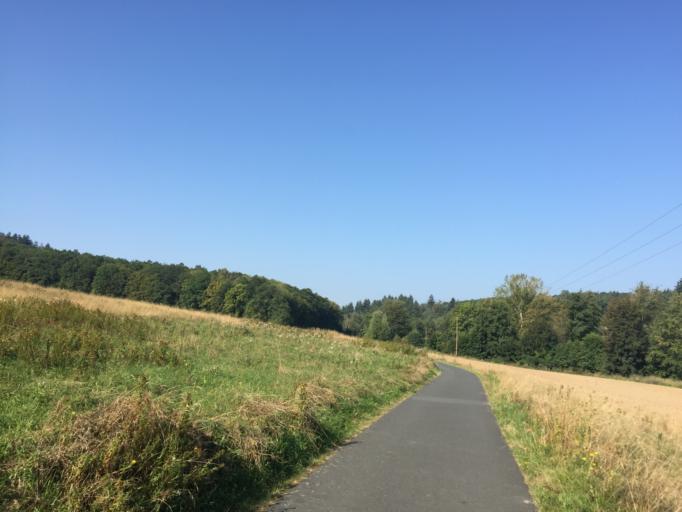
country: DE
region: Hesse
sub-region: Regierungsbezirk Giessen
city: Hoernsheim
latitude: 50.4598
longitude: 8.5754
